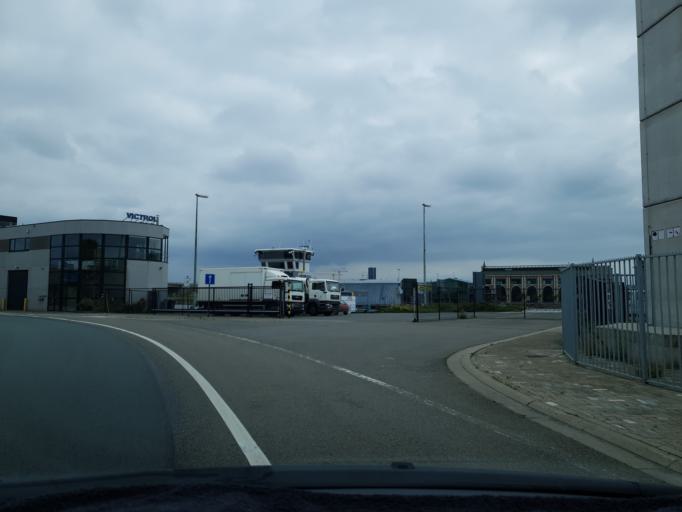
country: BE
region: Flanders
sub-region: Provincie Antwerpen
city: Antwerpen
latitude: 51.2433
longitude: 4.4088
